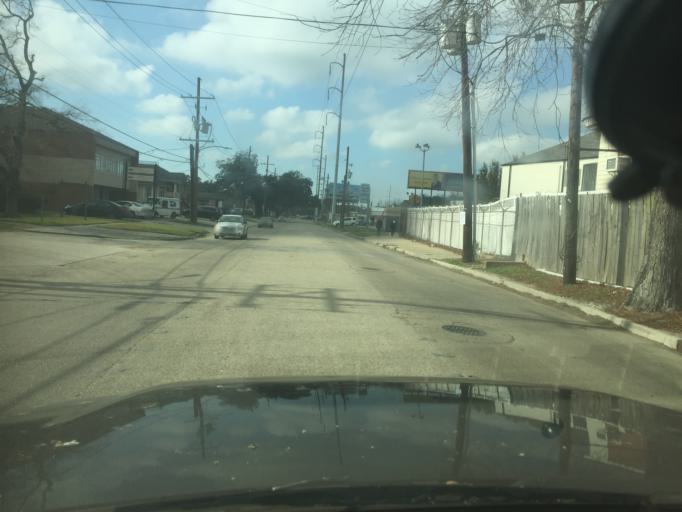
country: US
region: Louisiana
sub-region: Orleans Parish
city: New Orleans
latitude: 30.0026
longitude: -90.0409
